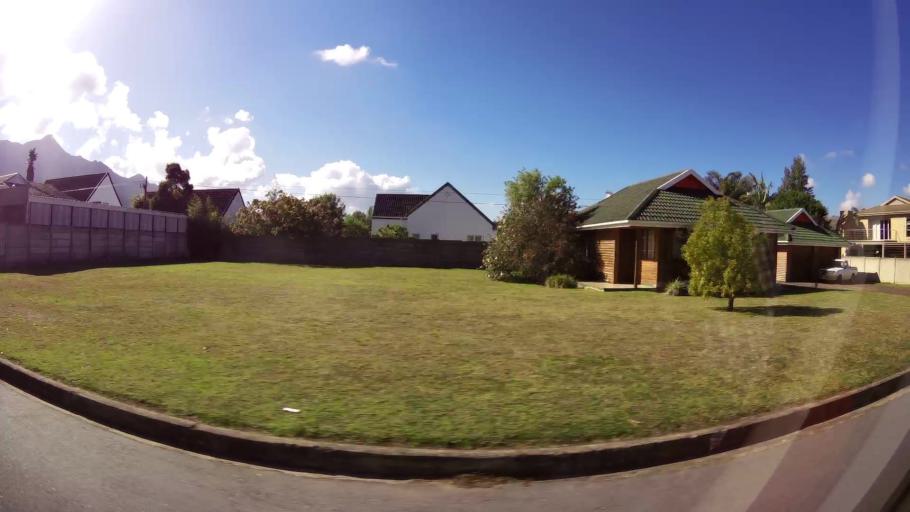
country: ZA
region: Western Cape
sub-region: Eden District Municipality
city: George
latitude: -33.9531
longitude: 22.4323
